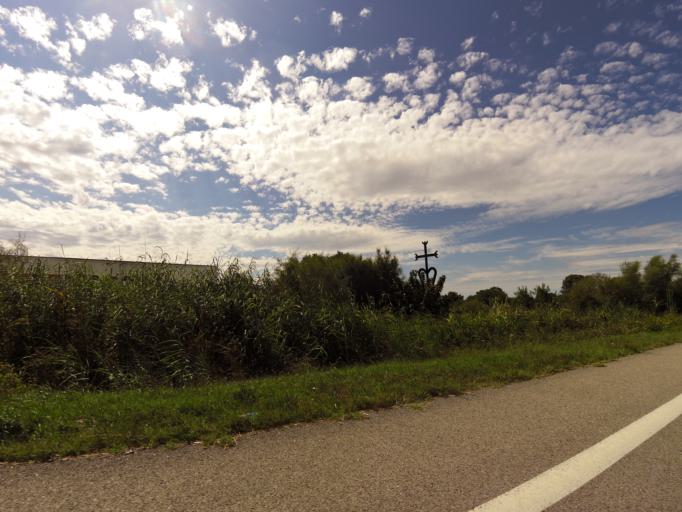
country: FR
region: Languedoc-Roussillon
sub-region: Departement du Gard
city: Aigues-Mortes
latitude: 43.5788
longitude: 4.1983
